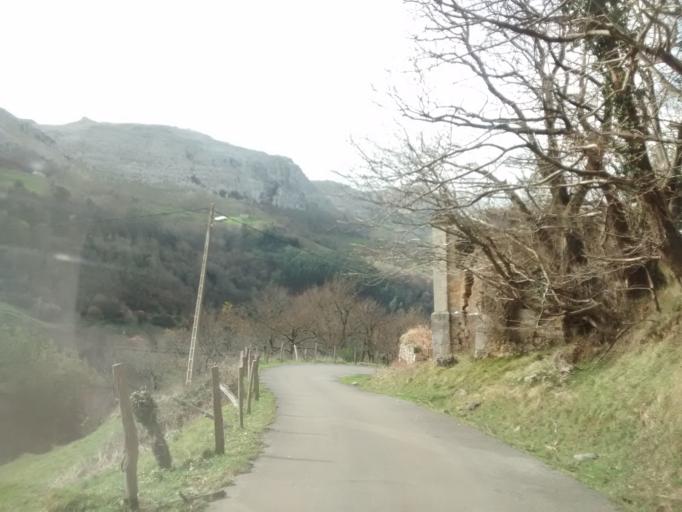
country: ES
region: Cantabria
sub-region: Provincia de Cantabria
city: Lierganes
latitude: 43.3220
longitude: -3.7132
